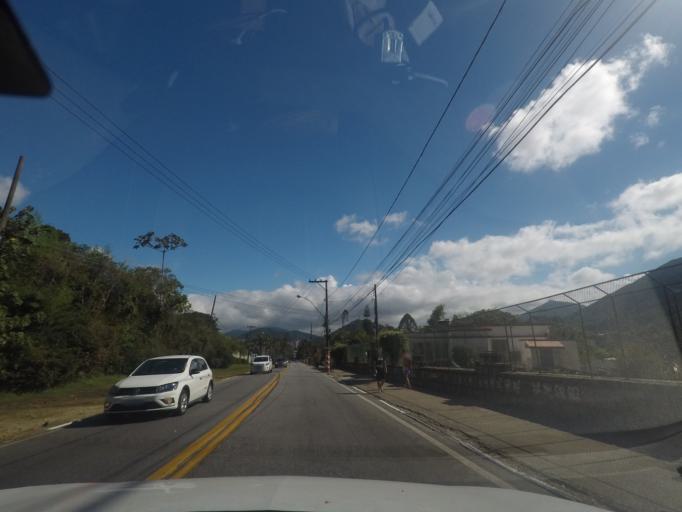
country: BR
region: Rio de Janeiro
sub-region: Teresopolis
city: Teresopolis
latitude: -22.4473
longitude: -42.9822
